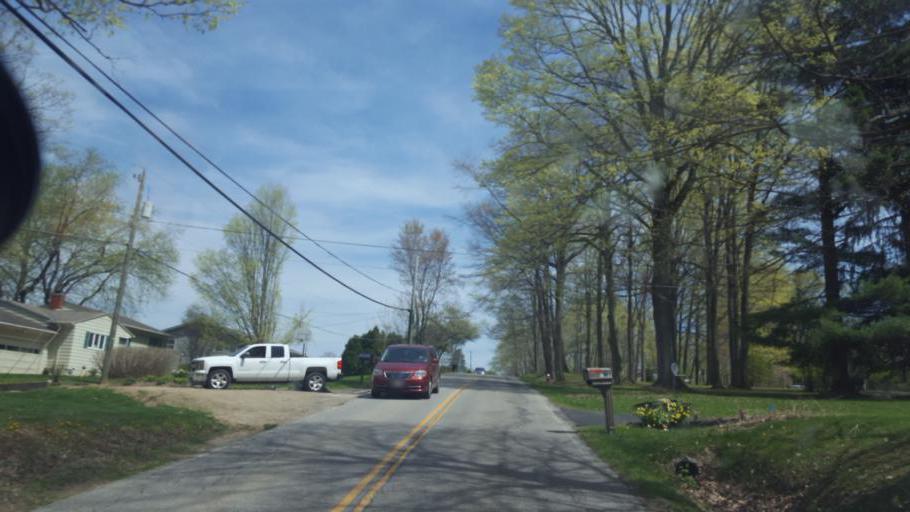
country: US
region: Ohio
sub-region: Richland County
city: Lexington
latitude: 40.6811
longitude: -82.5599
